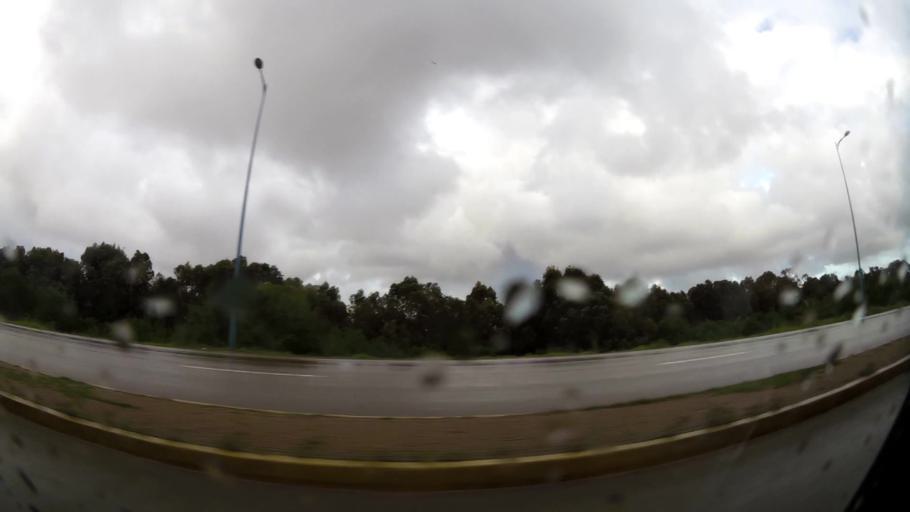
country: MA
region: Grand Casablanca
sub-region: Mohammedia
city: Mohammedia
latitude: 33.6731
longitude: -7.4071
